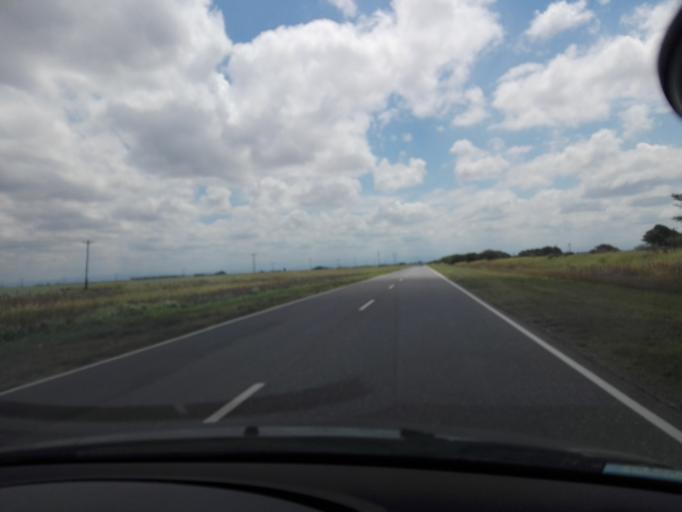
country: AR
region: Cordoba
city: Toledo
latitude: -31.6456
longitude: -64.0257
